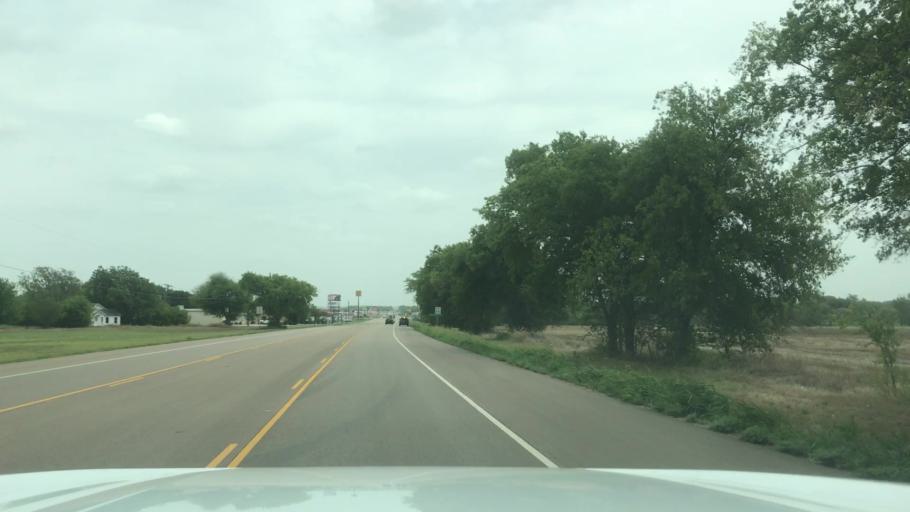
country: US
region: Texas
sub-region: McLennan County
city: Woodway
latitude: 31.5840
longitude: -97.3122
